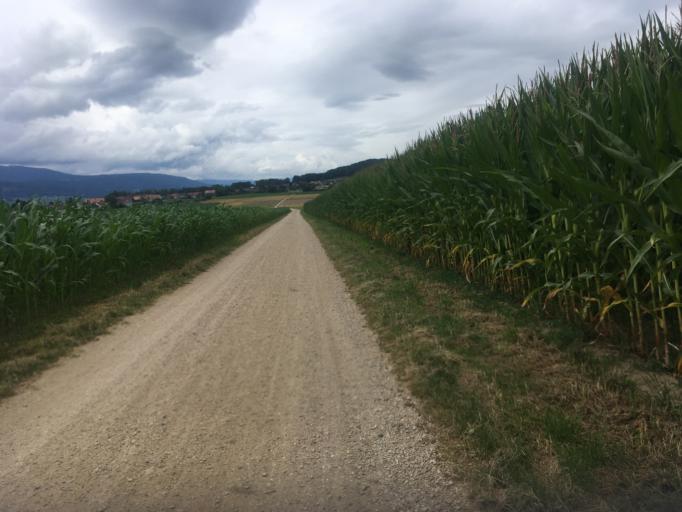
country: CH
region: Bern
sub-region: Seeland District
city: Ins
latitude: 47.0226
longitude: 7.1035
